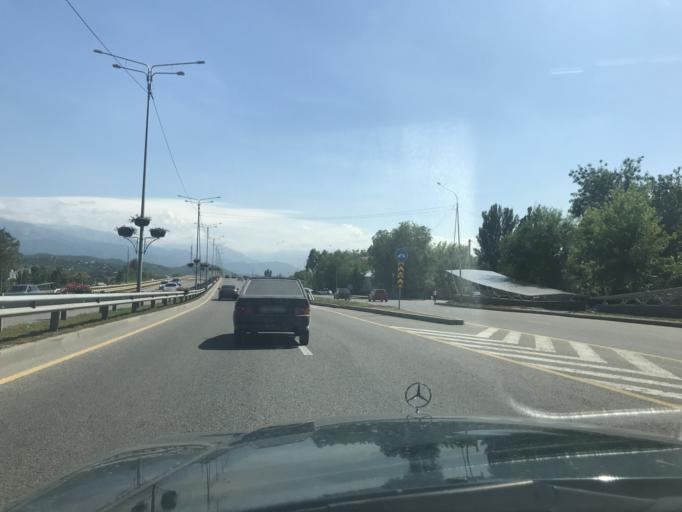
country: KZ
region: Almaty Qalasy
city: Almaty
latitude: 43.2871
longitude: 76.9878
